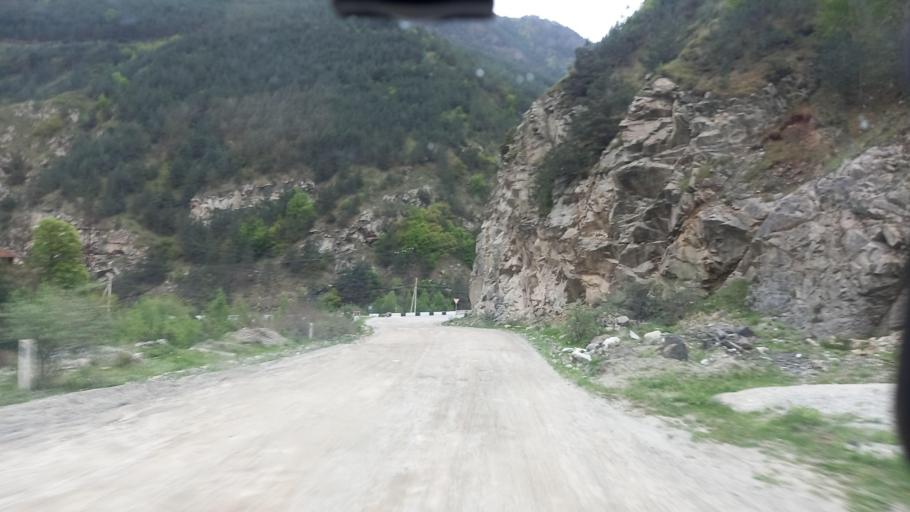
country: RU
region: North Ossetia
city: Mizur
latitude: 42.8400
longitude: 44.0268
